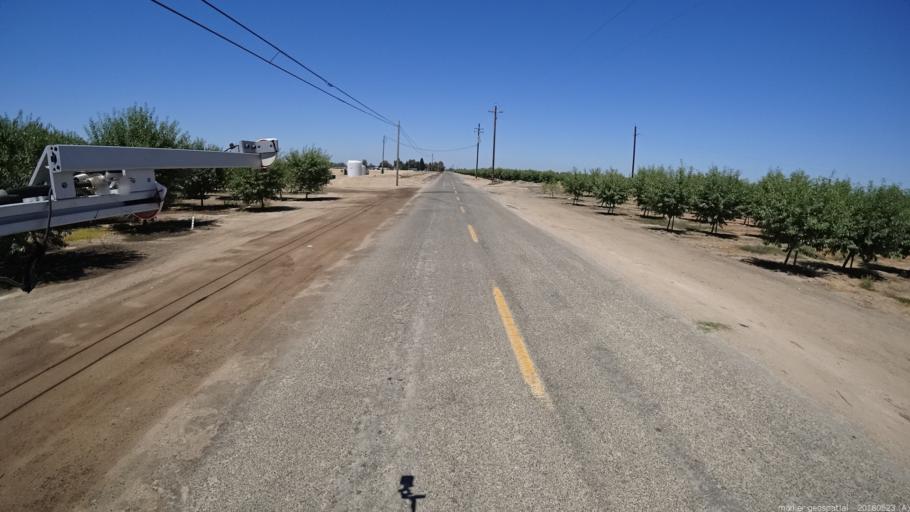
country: US
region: California
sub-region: Madera County
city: Chowchilla
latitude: 37.0910
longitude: -120.2426
